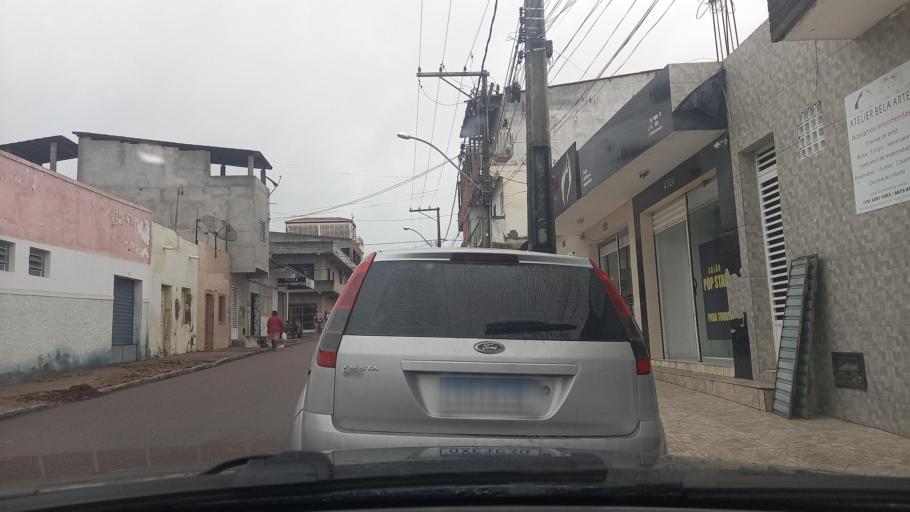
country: BR
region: Bahia
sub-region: Paulo Afonso
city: Paulo Afonso
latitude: -9.4066
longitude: -38.2218
